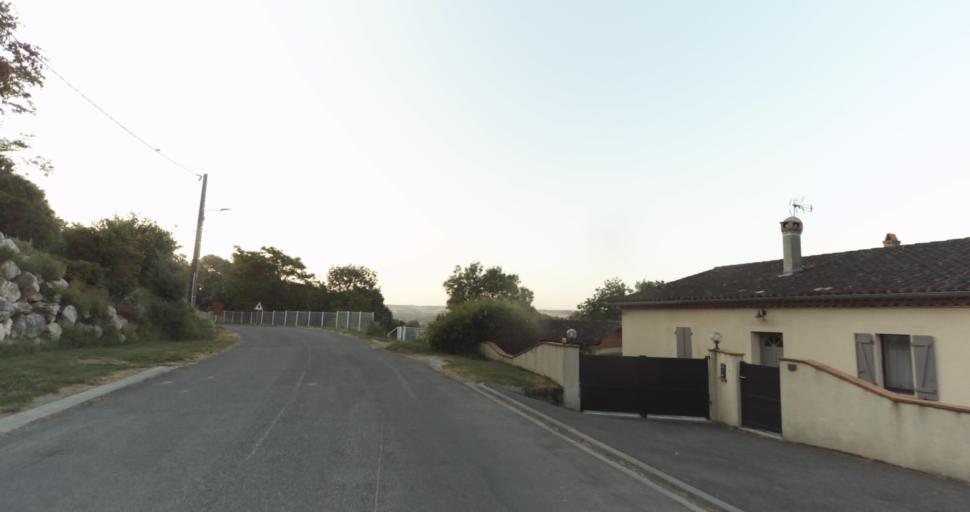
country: FR
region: Midi-Pyrenees
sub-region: Departement du Gers
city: Pujaudran
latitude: 43.6495
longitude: 1.1051
